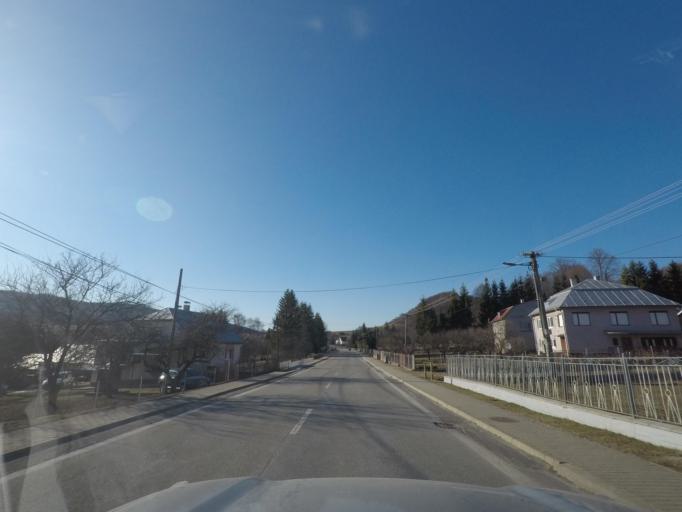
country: SK
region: Presovsky
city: Medzilaborce
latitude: 49.2271
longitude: 21.9669
